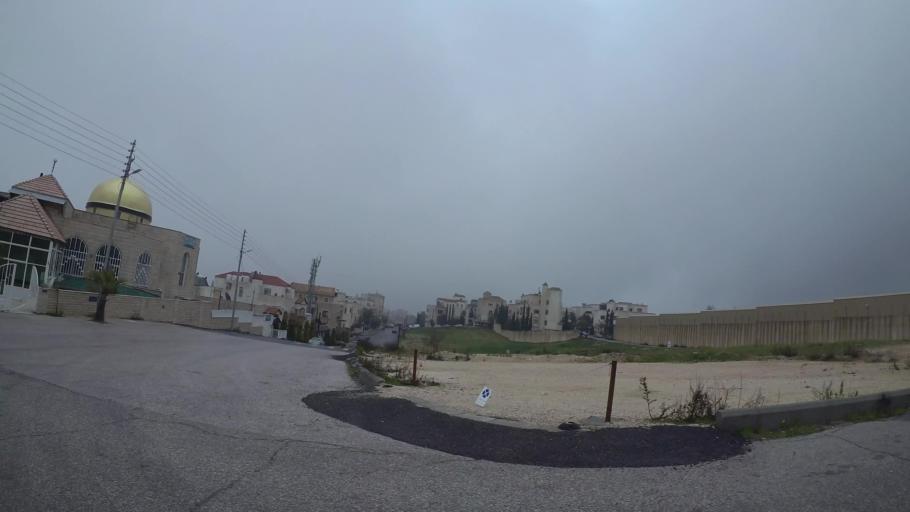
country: JO
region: Amman
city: Al Jubayhah
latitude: 32.0144
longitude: 35.8290
